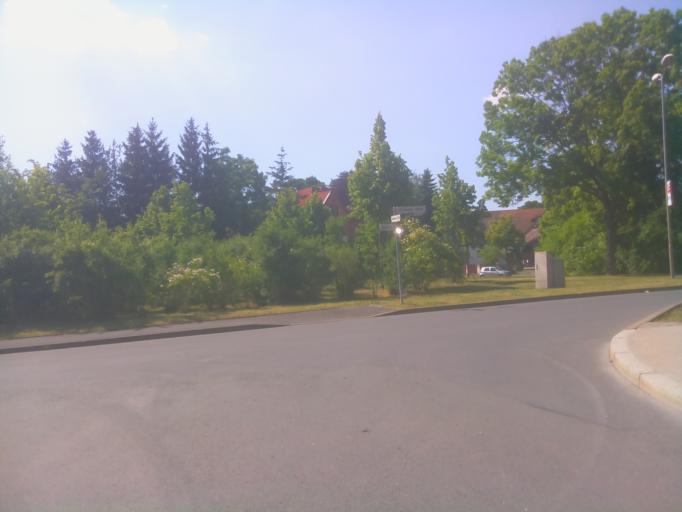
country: DE
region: Thuringia
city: Possneck
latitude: 50.7001
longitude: 11.6027
